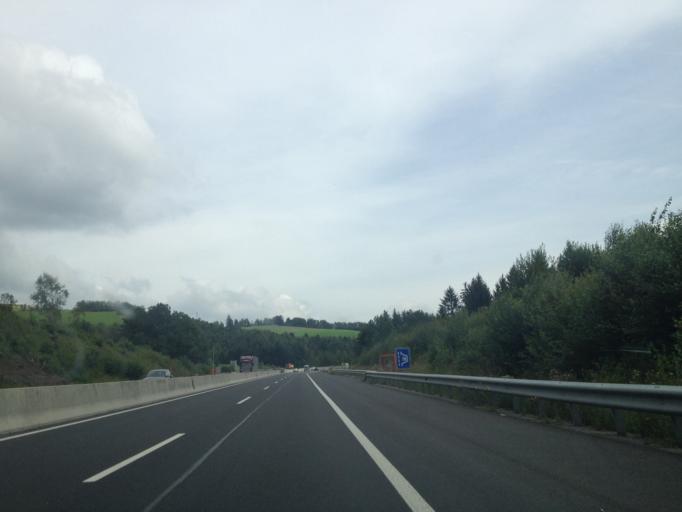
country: AT
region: Lower Austria
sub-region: Politischer Bezirk Neunkirchen
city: Zobern
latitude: 47.4956
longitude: 16.0996
